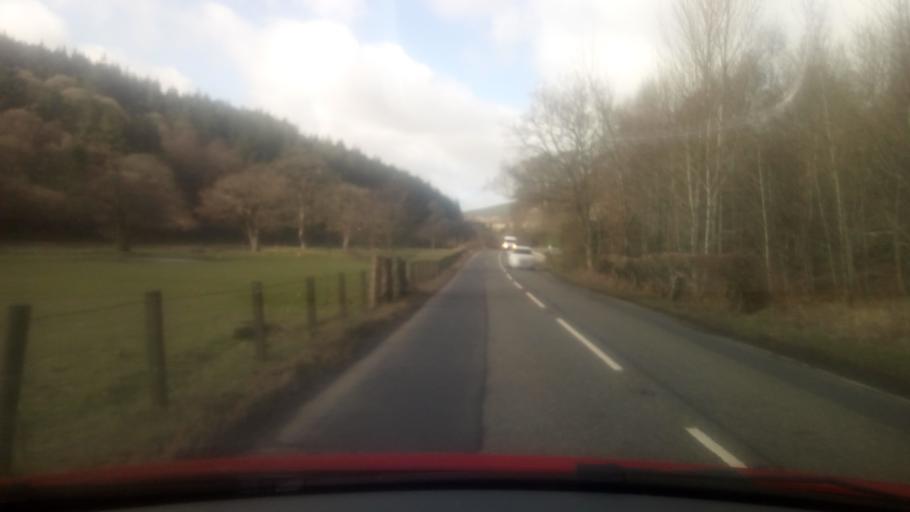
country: GB
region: Scotland
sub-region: The Scottish Borders
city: Innerleithen
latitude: 55.6268
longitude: -2.9681
